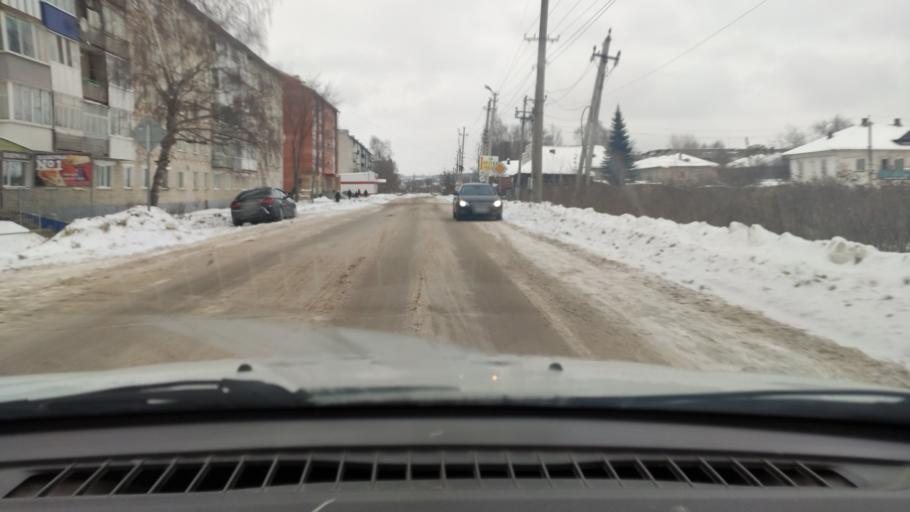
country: RU
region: Perm
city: Kungur
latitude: 57.4385
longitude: 56.9384
